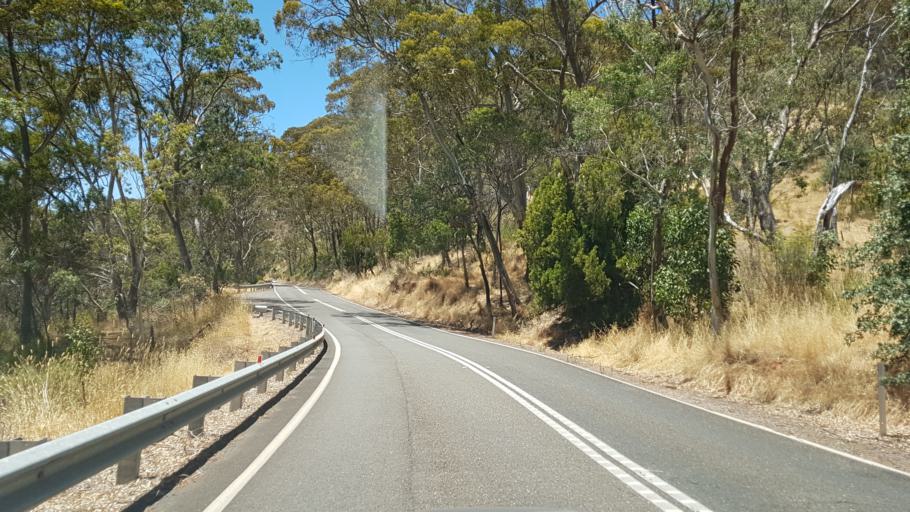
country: AU
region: South Australia
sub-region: Adelaide Hills
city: Gumeracha
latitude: -34.8435
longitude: 138.8366
